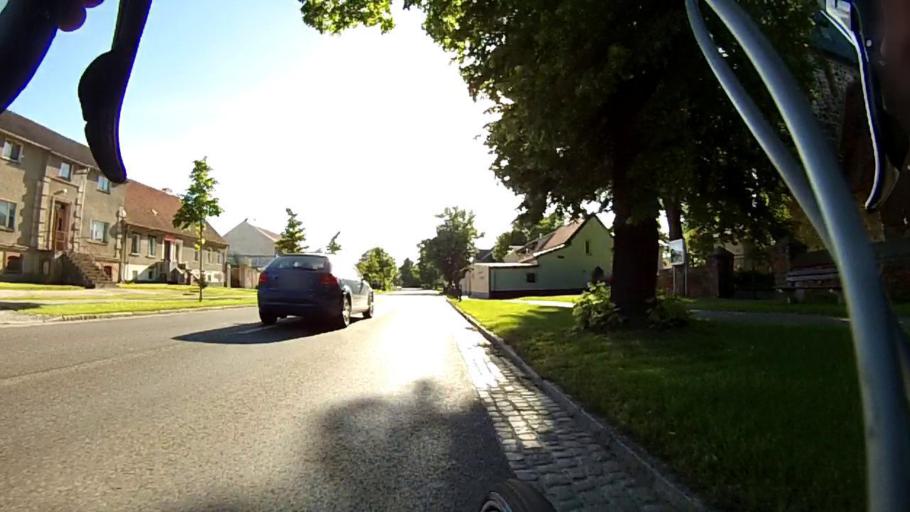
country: DE
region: Brandenburg
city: Werneuchen
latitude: 52.6224
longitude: 13.6776
